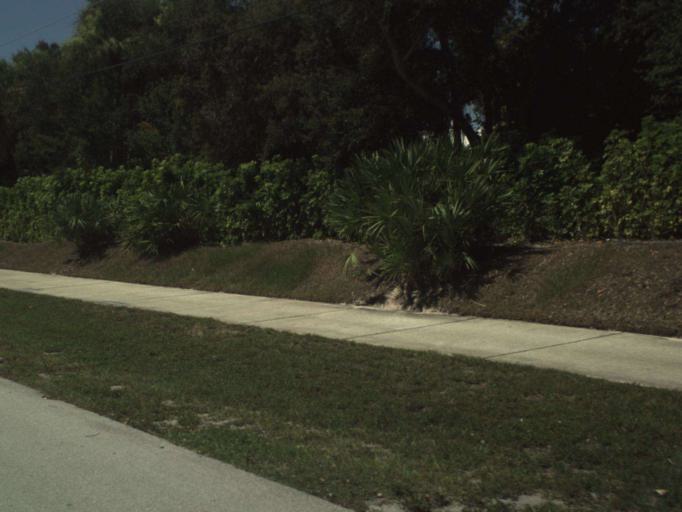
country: US
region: Florida
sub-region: Indian River County
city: South Beach
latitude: 27.6003
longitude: -80.3370
